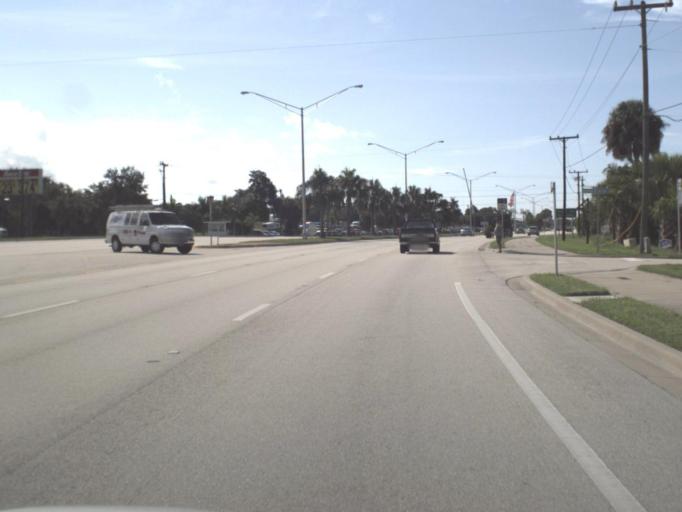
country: US
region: Florida
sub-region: Sarasota County
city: Laurel
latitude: 27.1310
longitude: -82.4539
